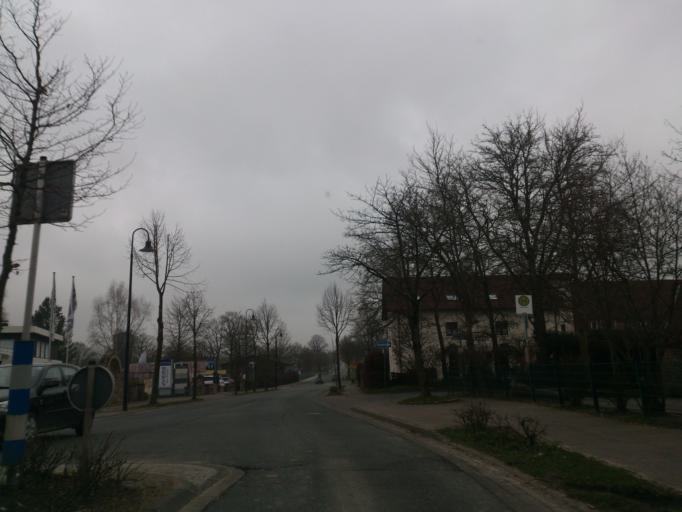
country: DE
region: North Rhine-Westphalia
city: Lichtenau
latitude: 51.6131
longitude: 8.8942
